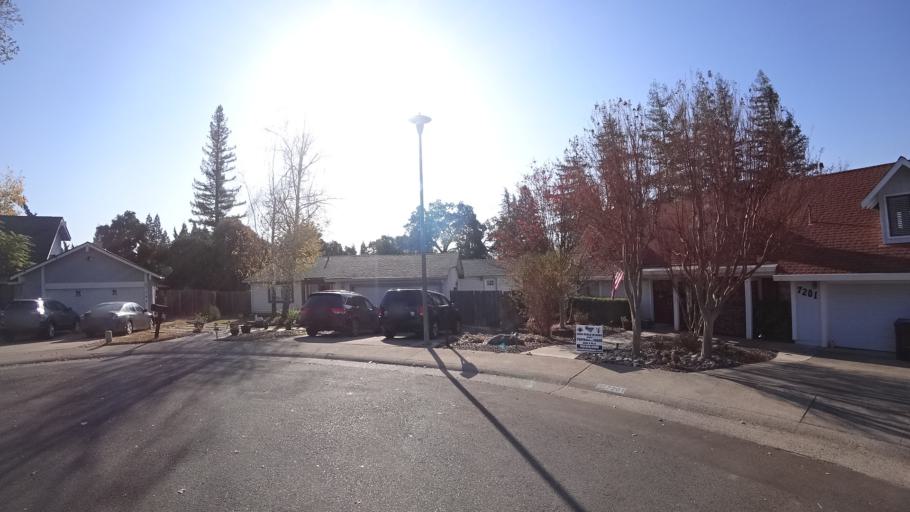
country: US
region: California
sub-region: Sacramento County
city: Orangevale
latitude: 38.6961
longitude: -121.2467
